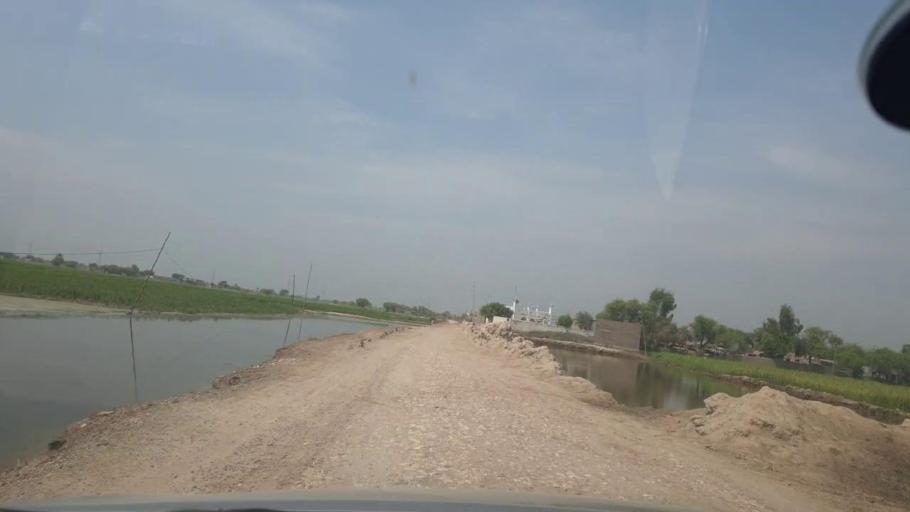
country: PK
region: Sindh
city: Thul
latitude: 28.1728
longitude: 68.6287
